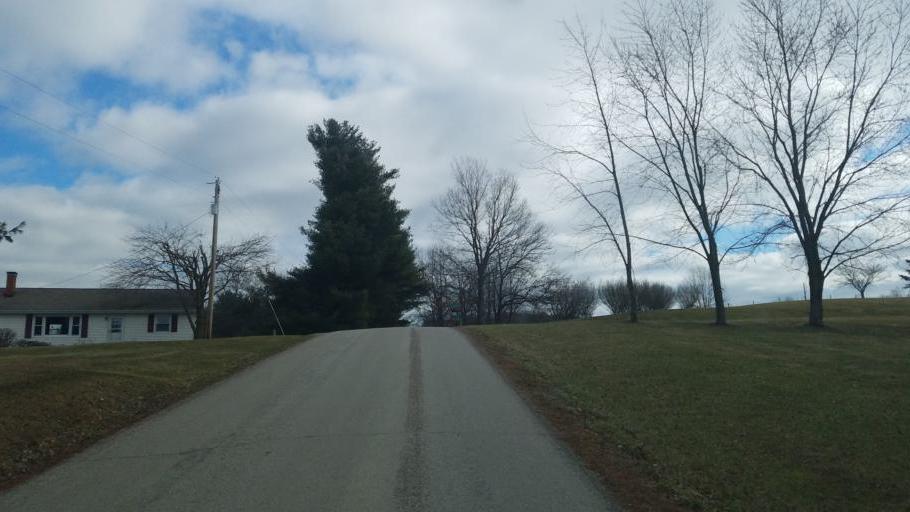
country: US
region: Ohio
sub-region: Knox County
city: Fredericktown
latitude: 40.5396
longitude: -82.4854
